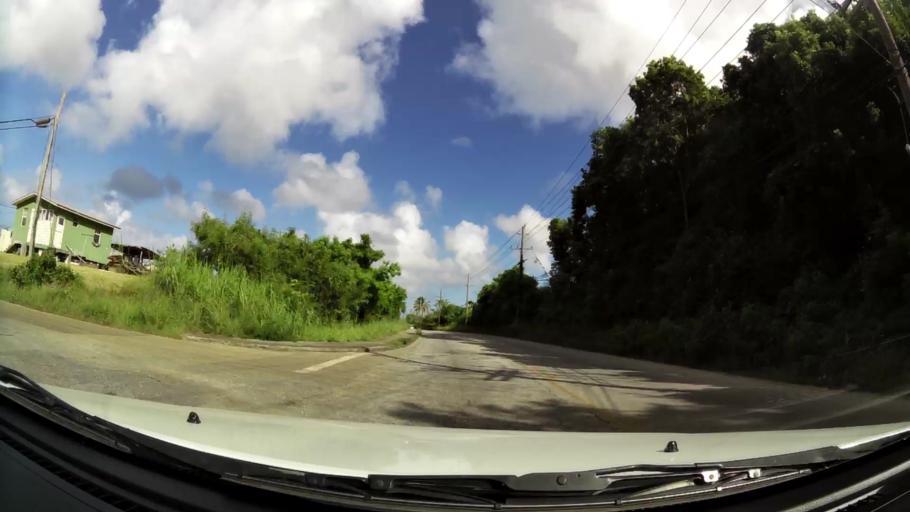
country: BB
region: Saint Peter
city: Speightstown
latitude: 13.2359
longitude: -59.6232
